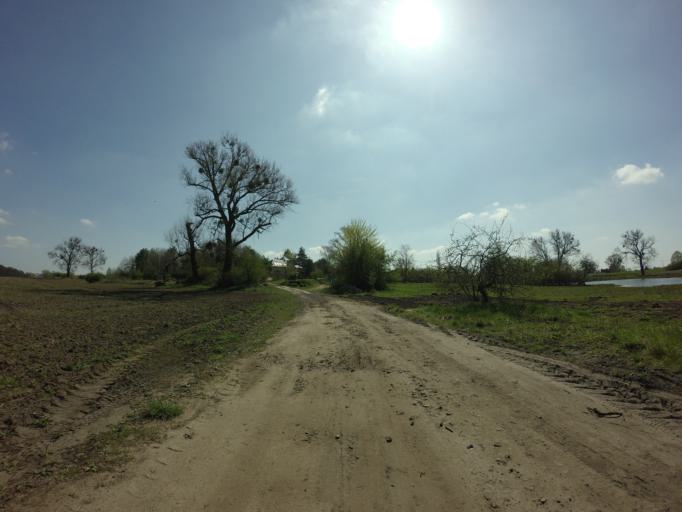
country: PL
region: West Pomeranian Voivodeship
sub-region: Powiat choszczenski
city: Choszczno
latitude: 53.1646
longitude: 15.4552
